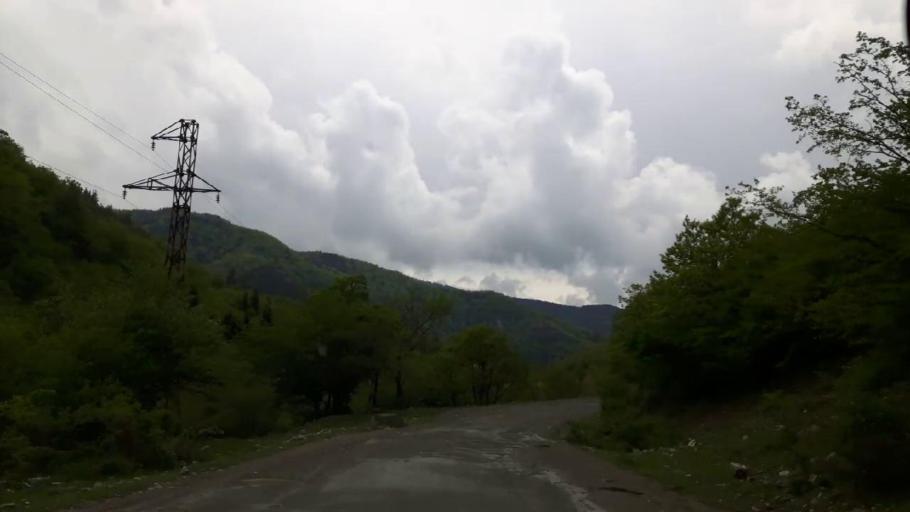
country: GE
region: Shida Kartli
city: Gori
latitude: 41.8734
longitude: 43.9876
